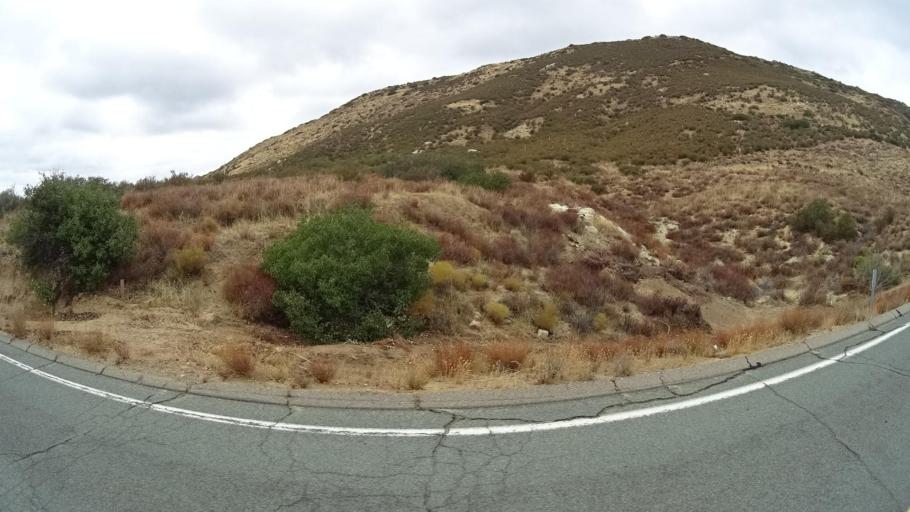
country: US
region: California
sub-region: San Diego County
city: Pine Valley
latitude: 32.7367
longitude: -116.4533
